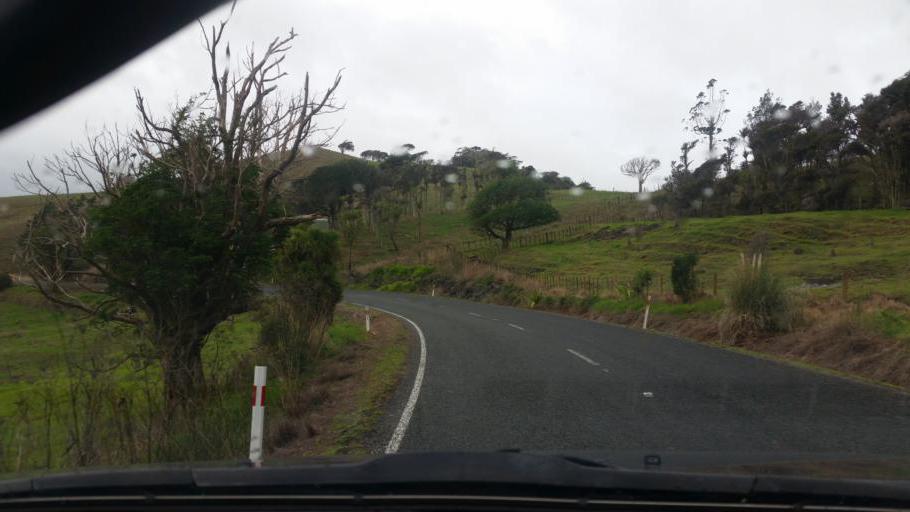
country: NZ
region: Northland
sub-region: Kaipara District
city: Dargaville
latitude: -36.0142
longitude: 173.9796
